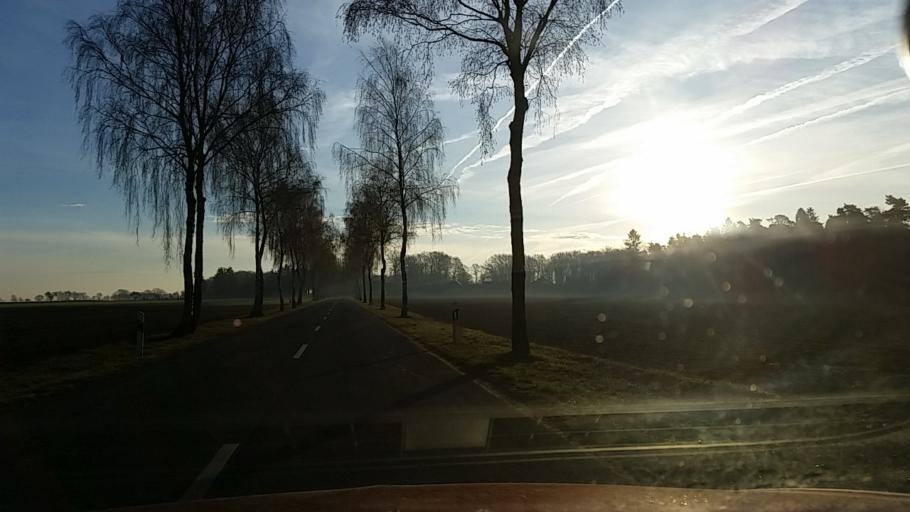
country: DE
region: Lower Saxony
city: Dedelstorf
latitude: 52.7316
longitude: 10.5347
